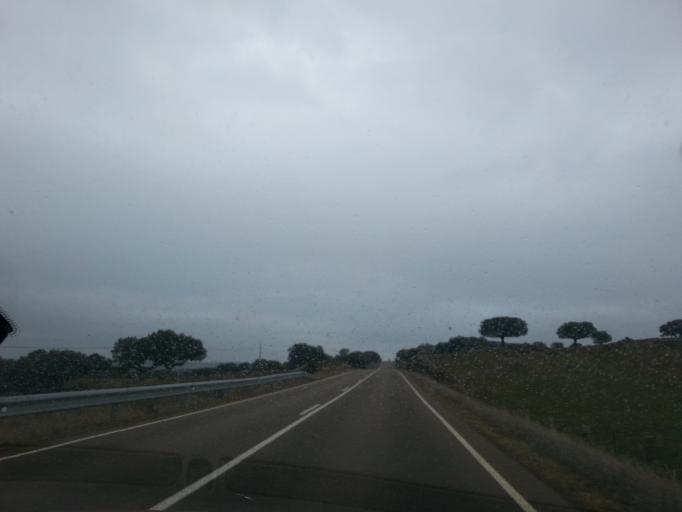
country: ES
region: Castille and Leon
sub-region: Provincia de Salamanca
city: Tamames
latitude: 40.6772
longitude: -6.0715
